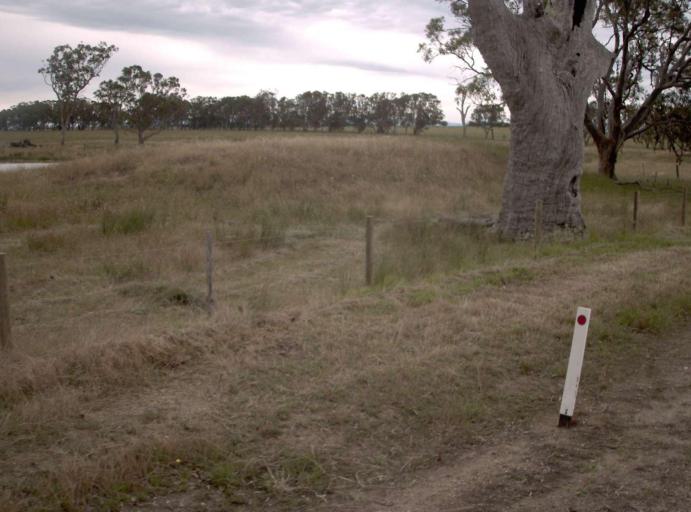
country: AU
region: Victoria
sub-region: Wellington
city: Sale
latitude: -38.0035
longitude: 147.1907
